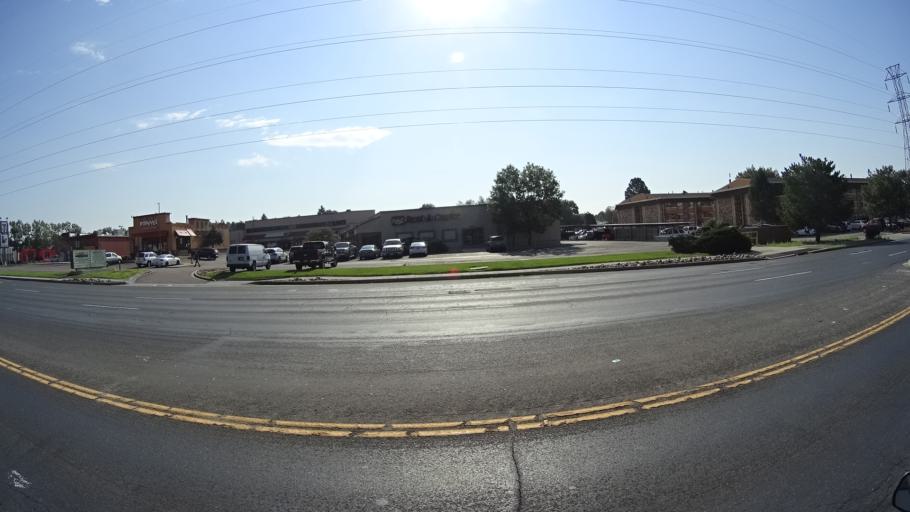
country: US
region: Colorado
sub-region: El Paso County
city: Stratmoor
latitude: 38.8312
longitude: -104.7574
